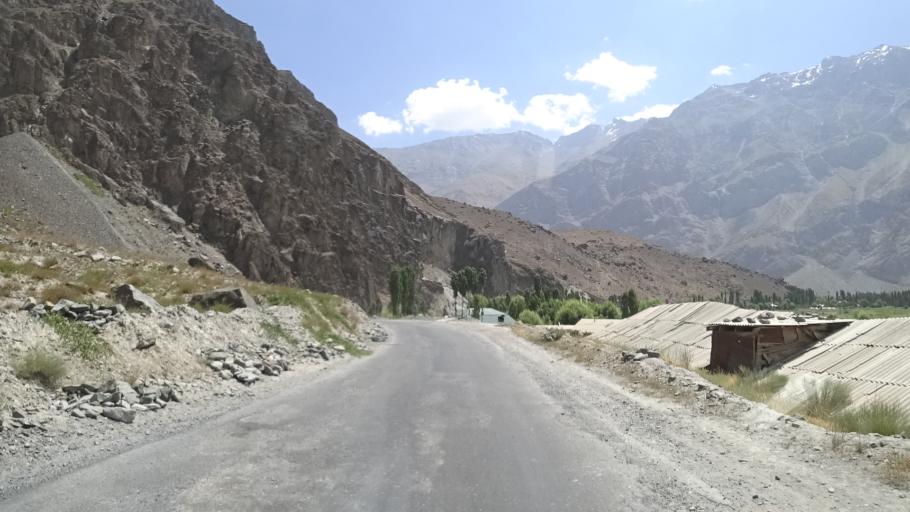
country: TJ
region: Gorno-Badakhshan
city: Rushon
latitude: 37.9456
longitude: 71.5897
